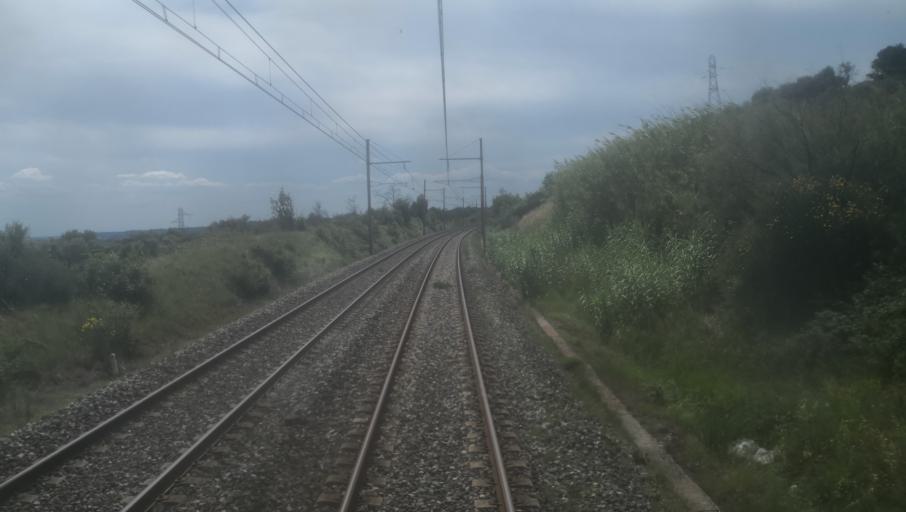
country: FR
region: Languedoc-Roussillon
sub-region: Departement du Gard
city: Jonquieres-Saint-Vincent
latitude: 43.7988
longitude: 4.5809
